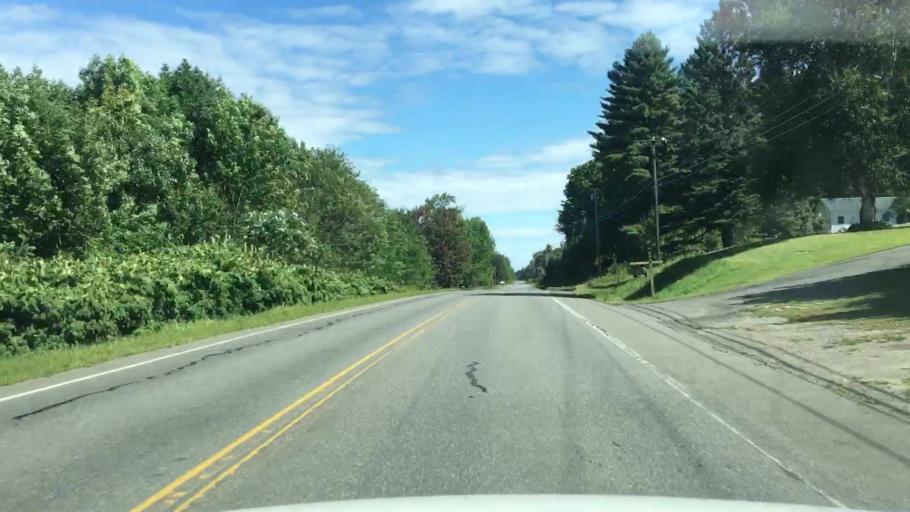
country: US
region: Maine
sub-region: Penobscot County
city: Dexter
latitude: 45.0597
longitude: -69.2511
